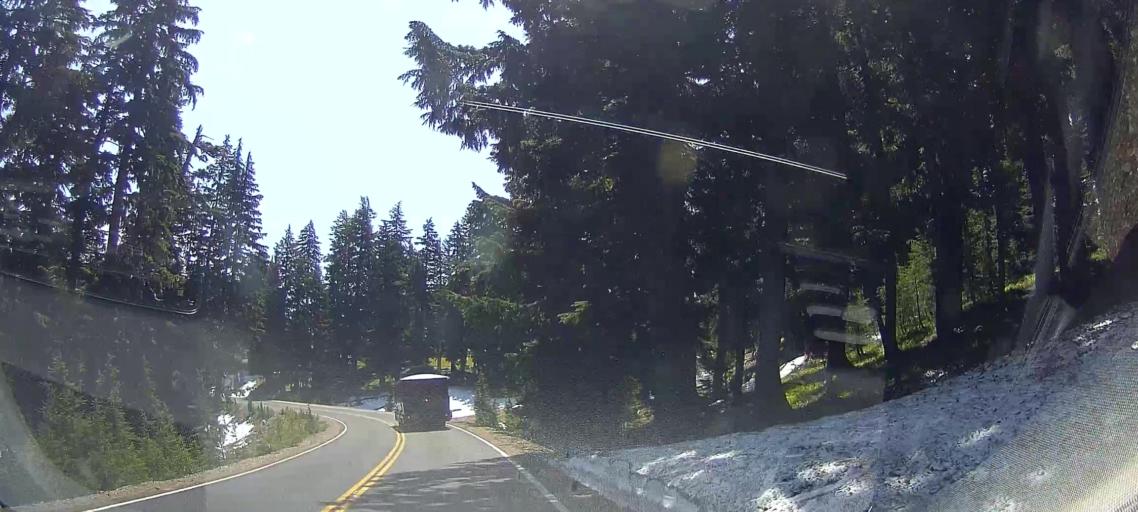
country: US
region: Oregon
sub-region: Jackson County
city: Shady Cove
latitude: 42.9804
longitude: -122.1214
